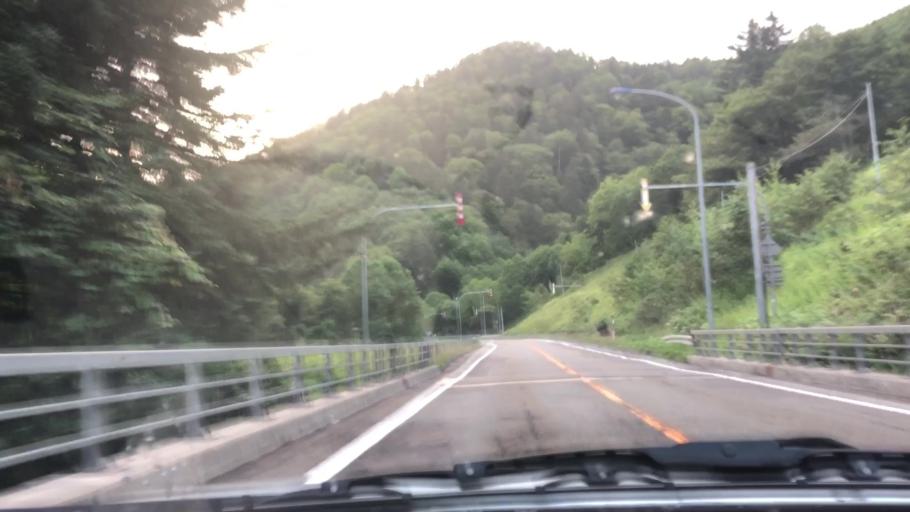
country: JP
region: Hokkaido
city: Shimo-furano
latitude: 42.9088
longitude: 142.3549
